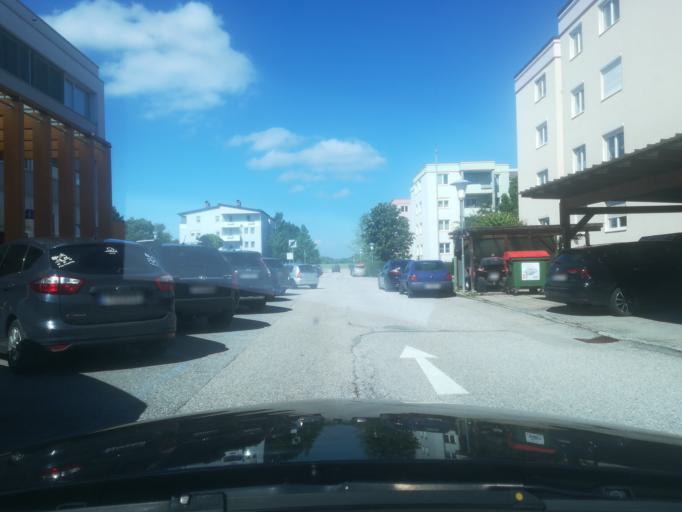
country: AT
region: Upper Austria
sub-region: Politischer Bezirk Perg
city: Perg
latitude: 48.2434
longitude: 14.6260
